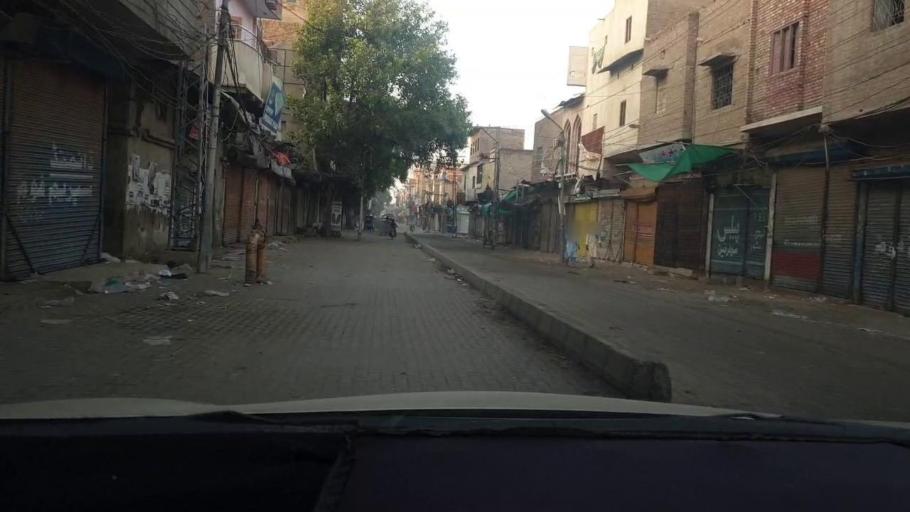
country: PK
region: Sindh
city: Larkana
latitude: 27.5565
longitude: 68.2161
